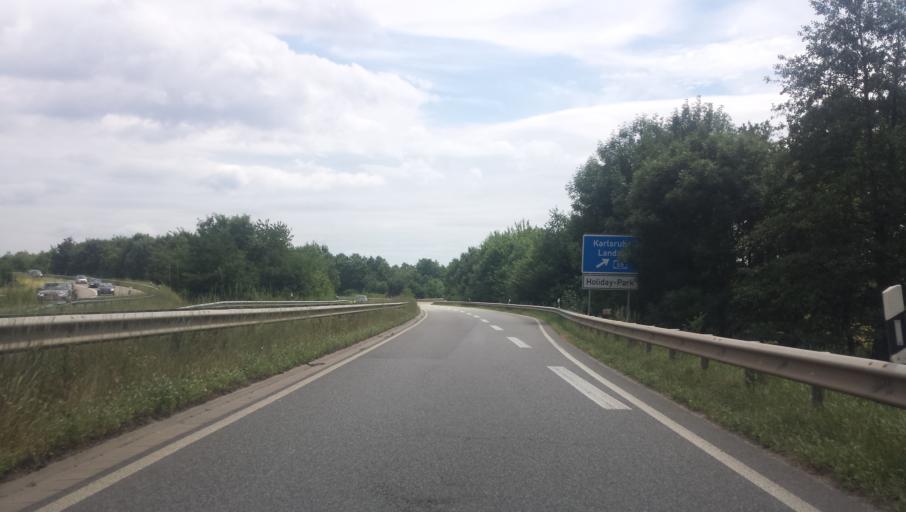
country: DE
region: Rheinland-Pfalz
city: Lachen-Speyerdorf
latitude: 49.3582
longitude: 8.1911
